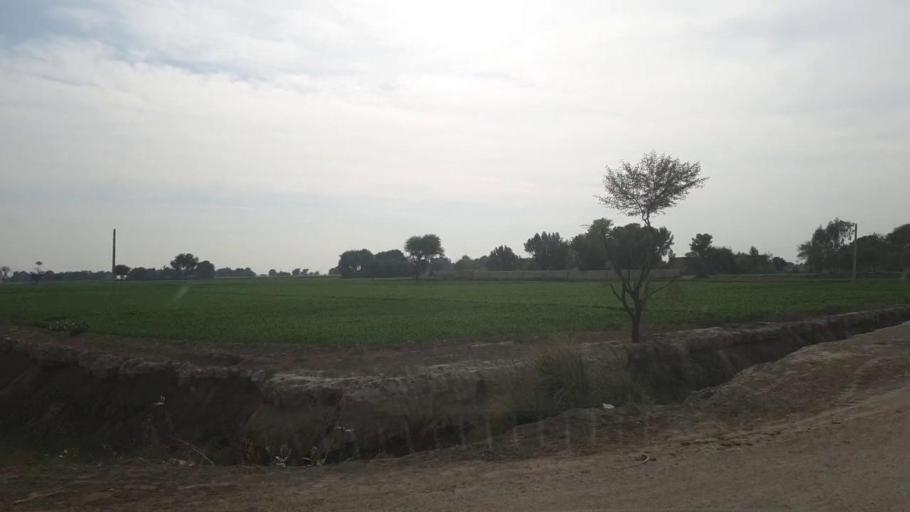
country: PK
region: Sindh
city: Shahpur Chakar
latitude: 26.1199
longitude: 68.5231
